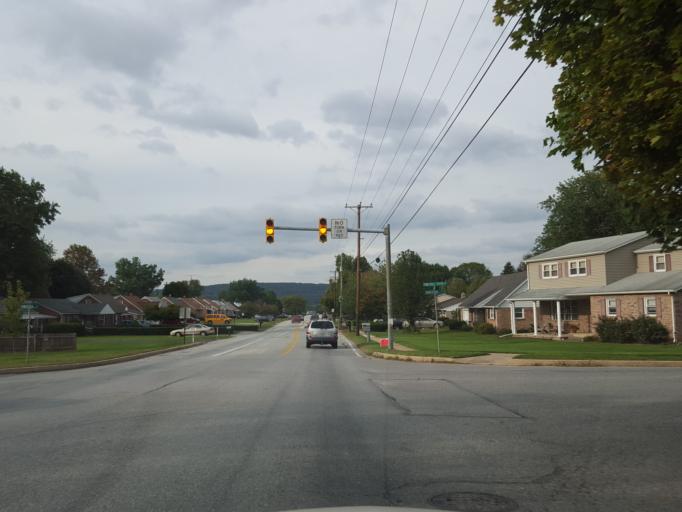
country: US
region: Pennsylvania
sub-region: York County
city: Stonybrook
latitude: 39.9700
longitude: -76.6597
